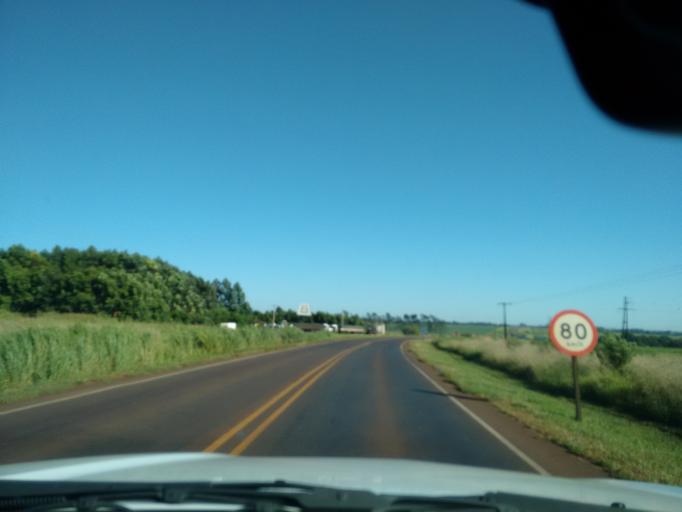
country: BR
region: Mato Grosso do Sul
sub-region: Dourados
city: Dourados
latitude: -22.3245
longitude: -54.8188
